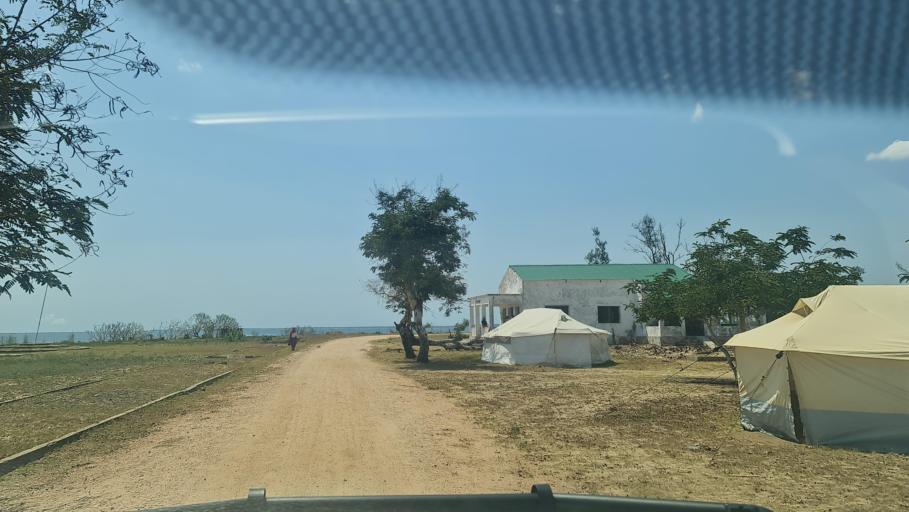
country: MZ
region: Nampula
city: Ilha de Mocambique
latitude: -15.1790
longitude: 40.5136
